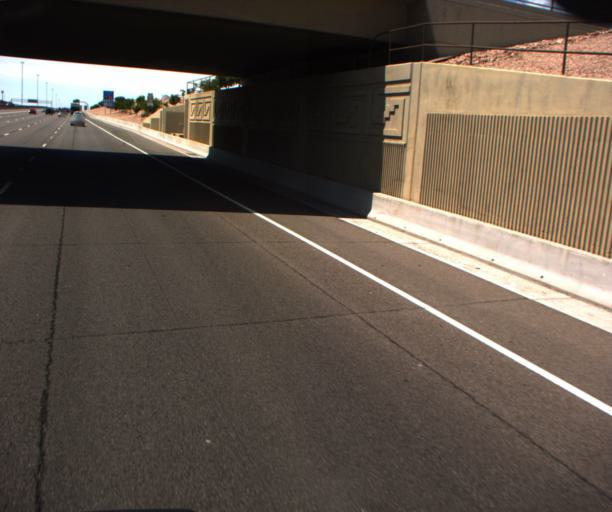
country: US
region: Arizona
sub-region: Maricopa County
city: Gilbert
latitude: 33.3866
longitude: -111.7622
